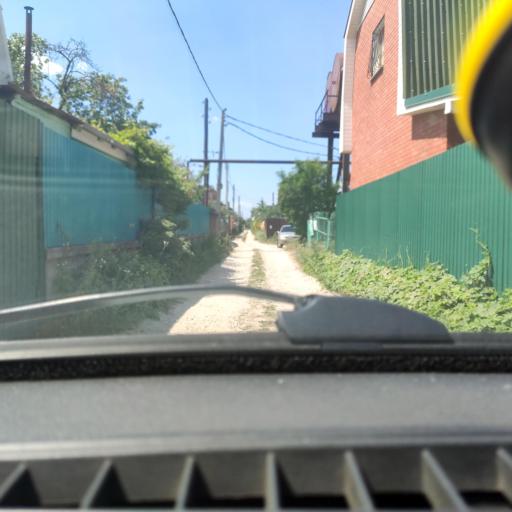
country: RU
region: Samara
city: Zhigulevsk
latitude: 53.4562
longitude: 49.5287
